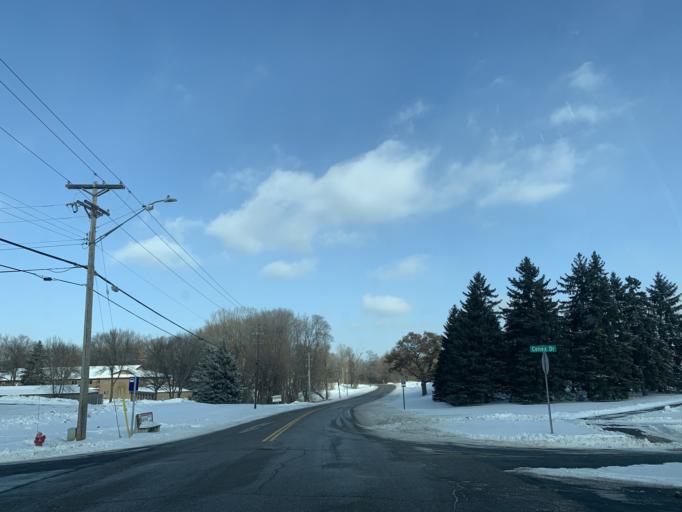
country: US
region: Minnesota
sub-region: Dakota County
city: Inver Grove Heights
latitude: 44.8690
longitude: -93.0659
